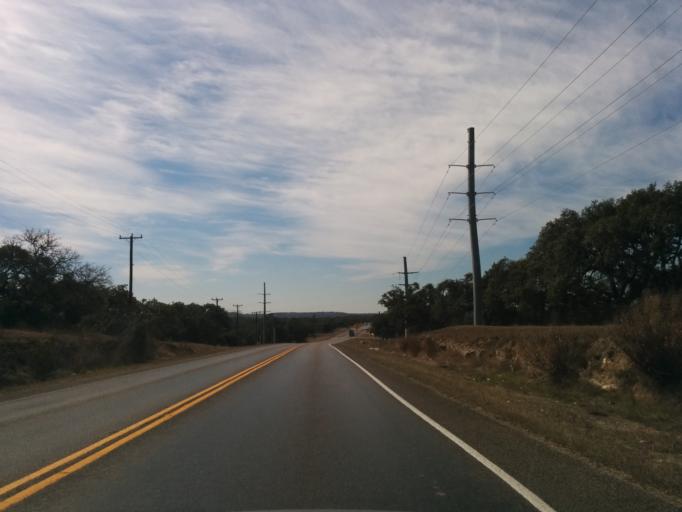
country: US
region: Texas
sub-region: Bexar County
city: Fair Oaks Ranch
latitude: 29.7633
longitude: -98.6106
